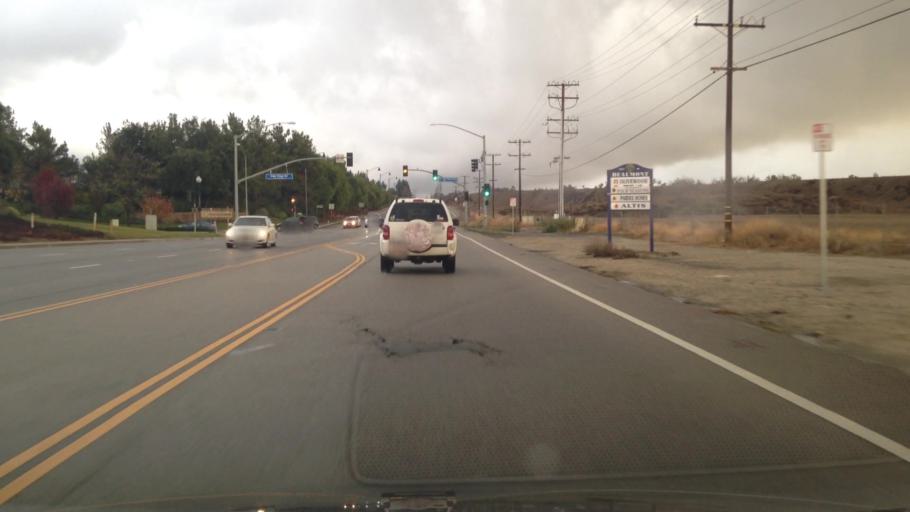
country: US
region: California
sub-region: Riverside County
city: Beaumont
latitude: 33.9470
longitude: -116.9967
